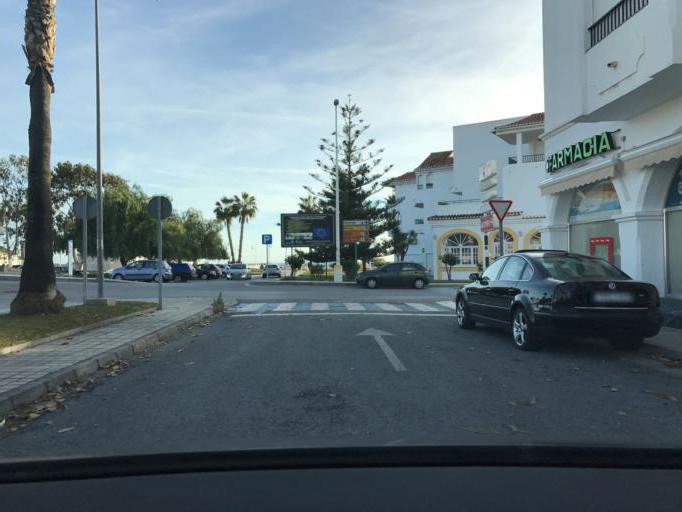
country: ES
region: Andalusia
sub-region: Provincia de Granada
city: El Varadero
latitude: 36.7241
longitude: -3.5355
